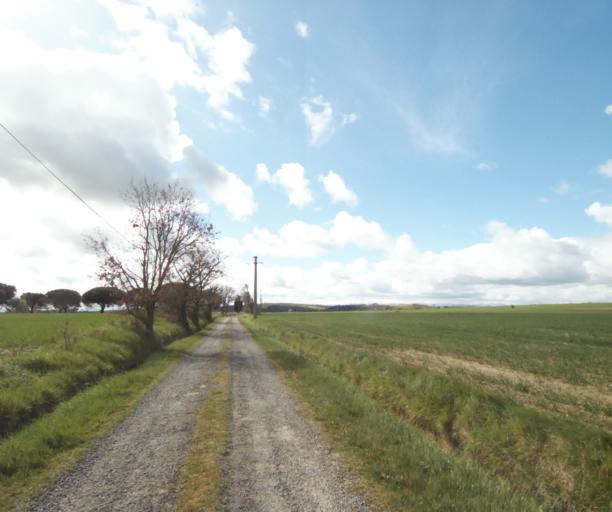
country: FR
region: Midi-Pyrenees
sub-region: Departement de l'Ariege
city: Saverdun
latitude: 43.2380
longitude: 1.5481
